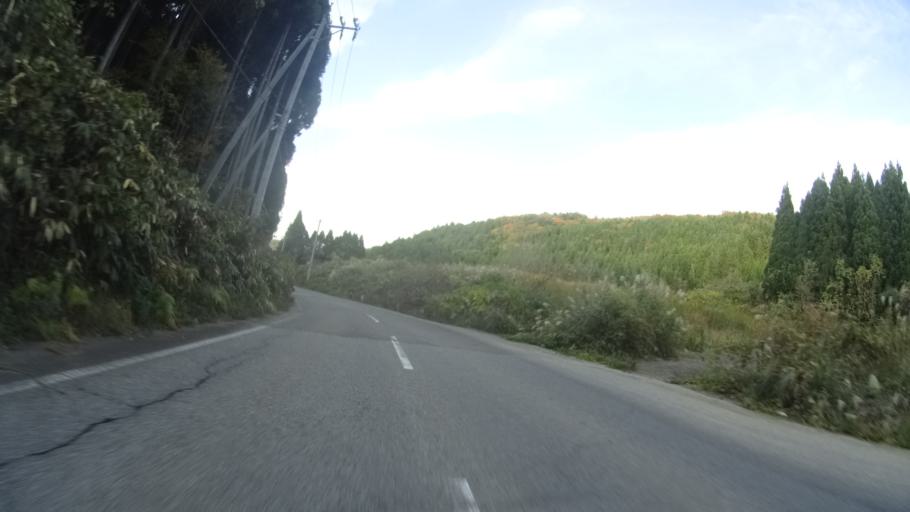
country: JP
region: Ishikawa
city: Nanao
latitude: 37.2077
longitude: 136.7080
